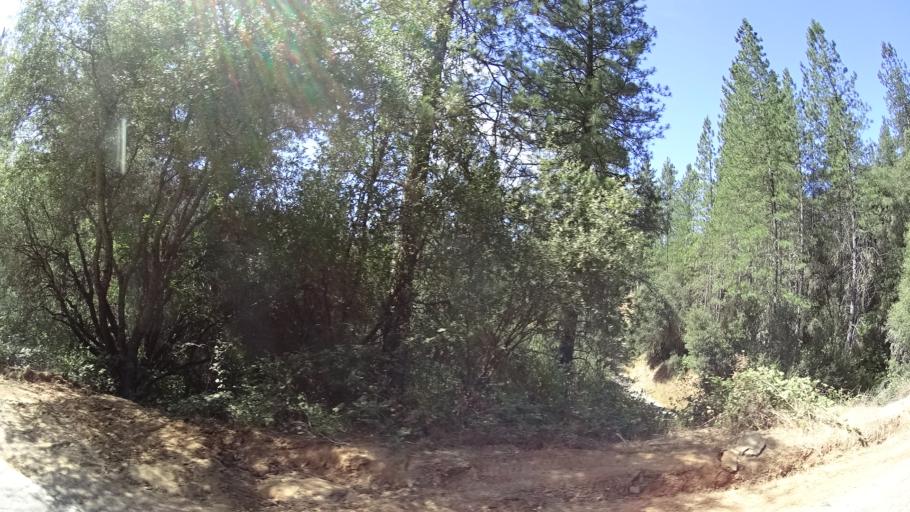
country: US
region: California
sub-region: Amador County
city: Pioneer
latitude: 38.3651
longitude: -120.5055
